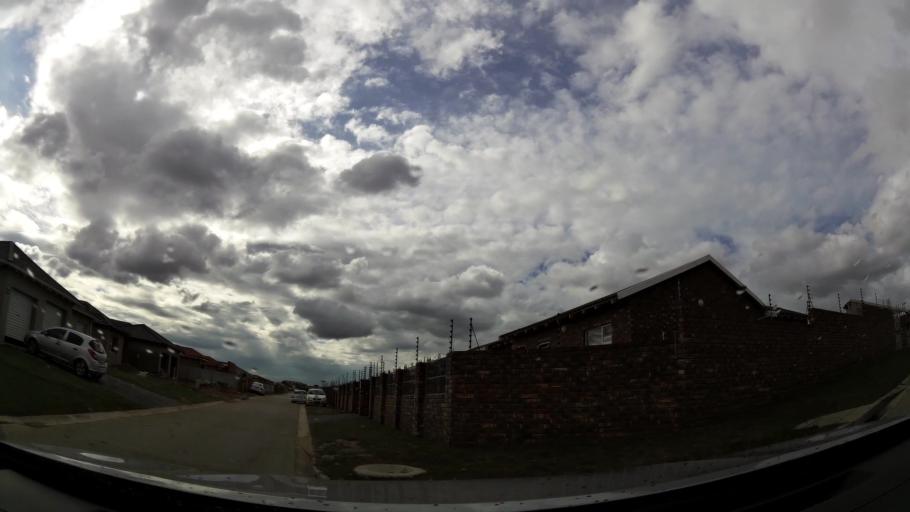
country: ZA
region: Eastern Cape
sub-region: Nelson Mandela Bay Metropolitan Municipality
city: Port Elizabeth
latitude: -33.9304
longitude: 25.5071
